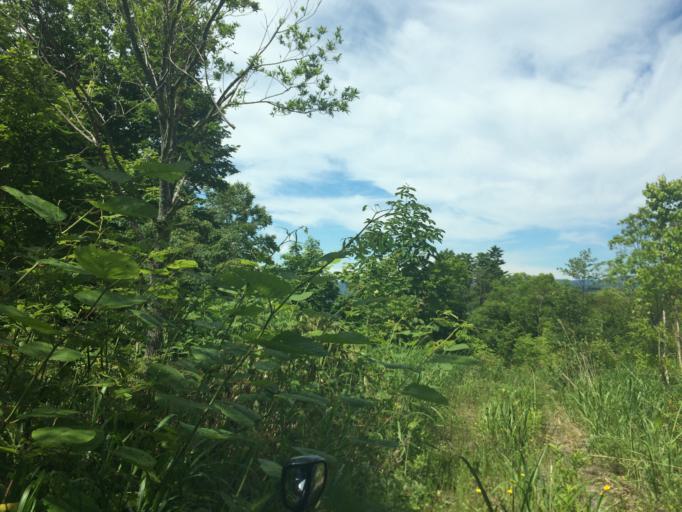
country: JP
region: Hokkaido
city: Niseko Town
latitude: 42.8622
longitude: 140.8194
